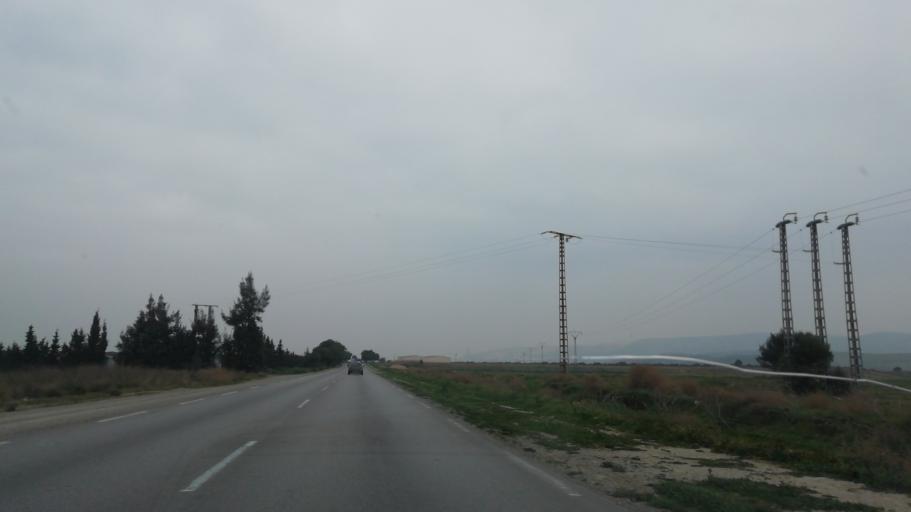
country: DZ
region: Mascara
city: Sig
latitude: 35.5386
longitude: -0.3547
